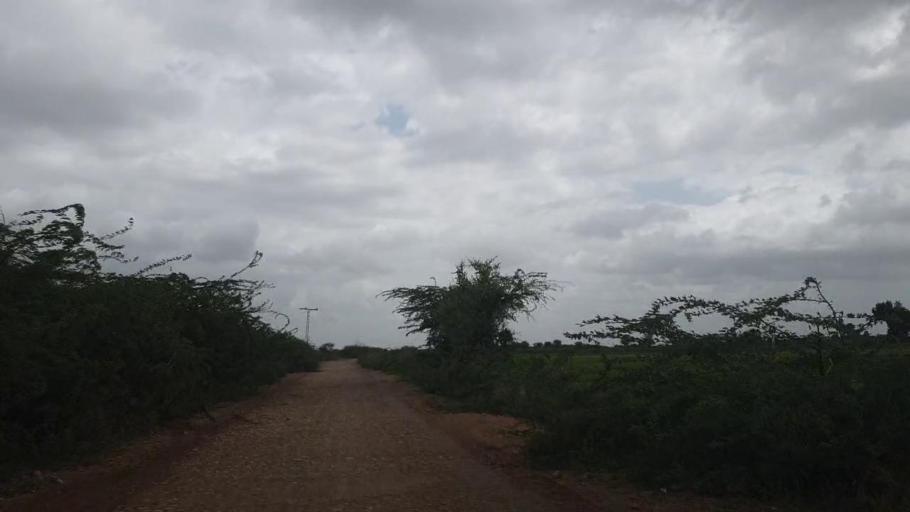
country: PK
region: Sindh
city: Badin
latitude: 24.6525
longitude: 68.9459
